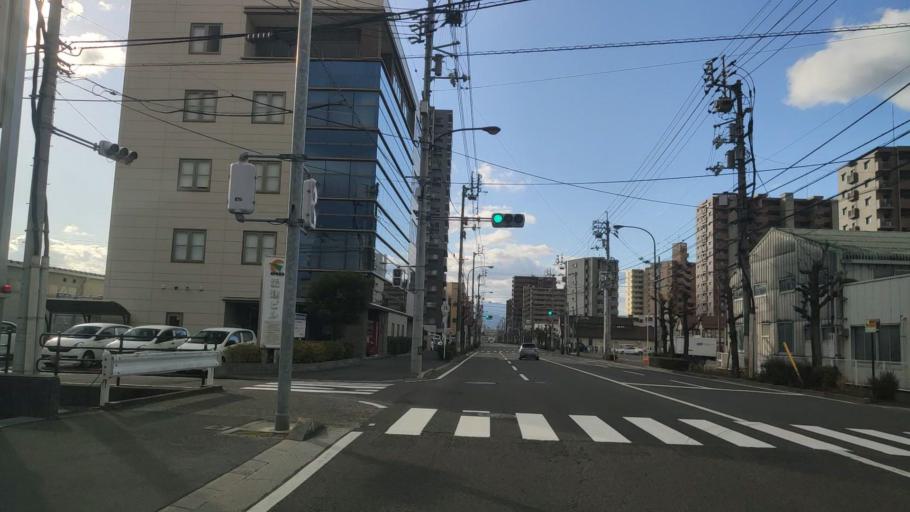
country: JP
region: Ehime
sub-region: Shikoku-chuo Shi
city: Matsuyama
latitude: 33.8356
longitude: 132.7525
